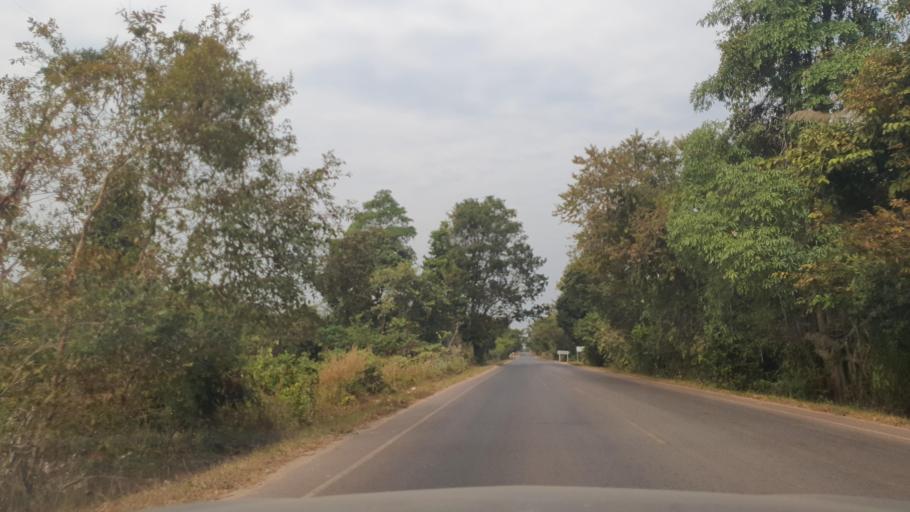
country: TH
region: Changwat Bueng Kan
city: Bung Khla
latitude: 18.2295
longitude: 104.0310
